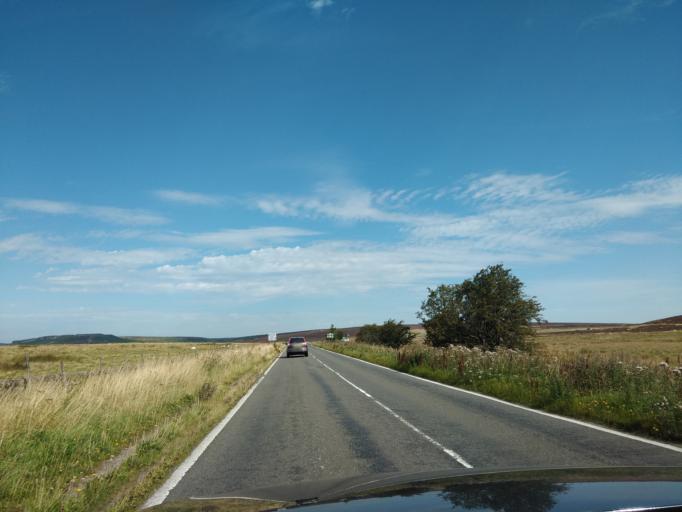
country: GB
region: England
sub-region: Derbyshire
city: Hathersage
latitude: 53.3096
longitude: -1.5991
